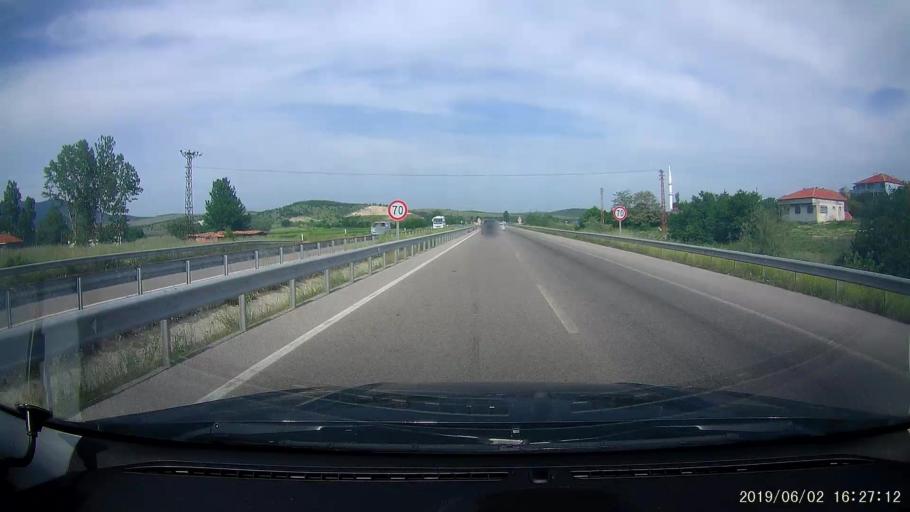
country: TR
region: Samsun
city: Ladik
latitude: 41.0017
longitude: 35.8216
